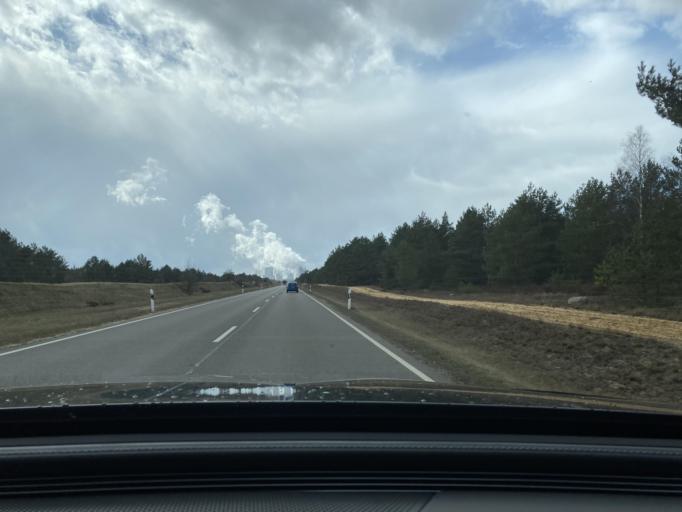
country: DE
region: Saxony
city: Boxberg
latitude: 51.4282
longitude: 14.6460
